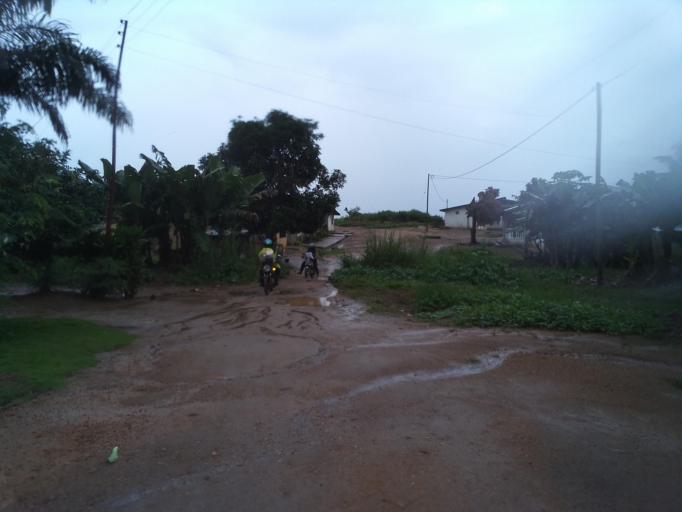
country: SL
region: Eastern Province
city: Kenema
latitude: 7.8536
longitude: -11.1926
